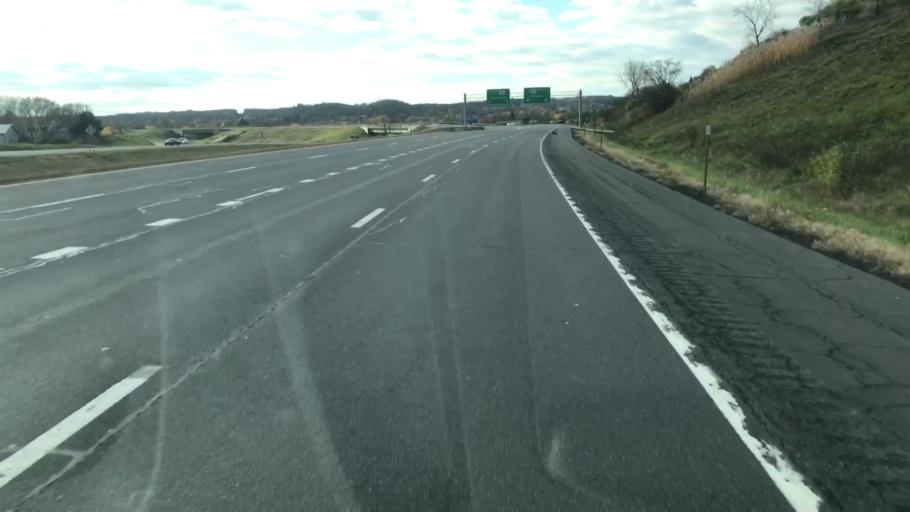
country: US
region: New York
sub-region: Onondaga County
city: Fairmount
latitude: 43.0612
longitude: -76.2364
